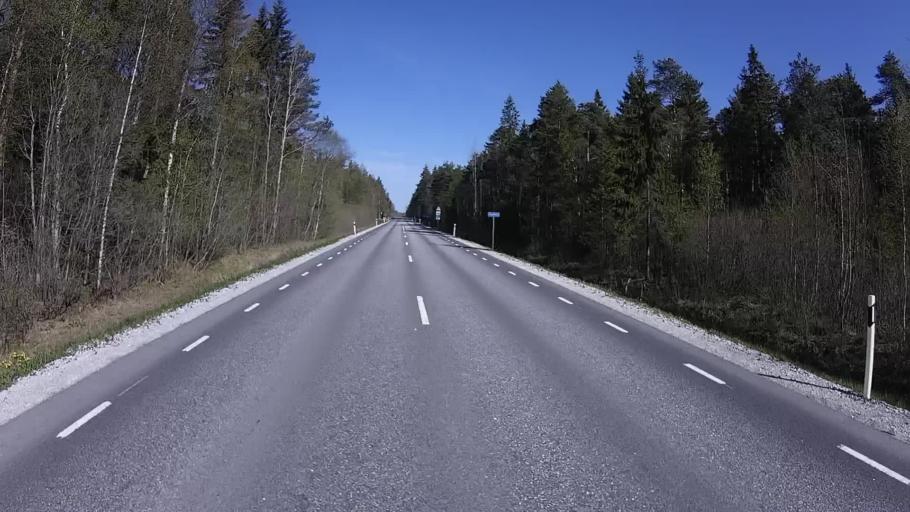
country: EE
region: Raplamaa
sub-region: Jaervakandi vald
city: Jarvakandi
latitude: 58.8582
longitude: 24.7902
